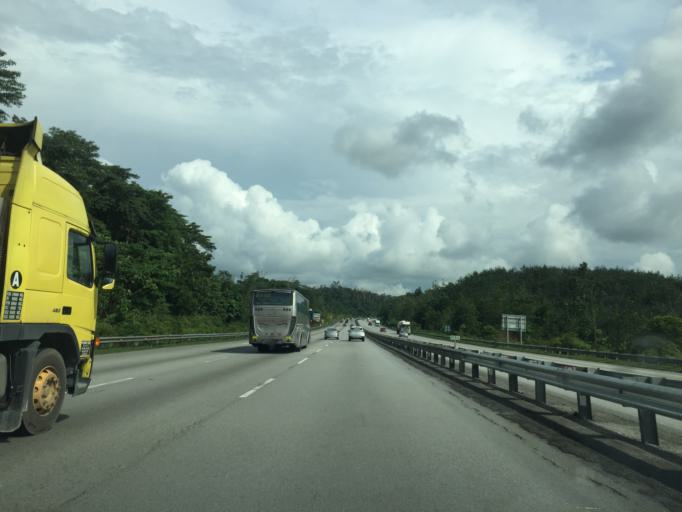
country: MY
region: Selangor
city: Batang Berjuntai
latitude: 3.5477
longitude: 101.5185
